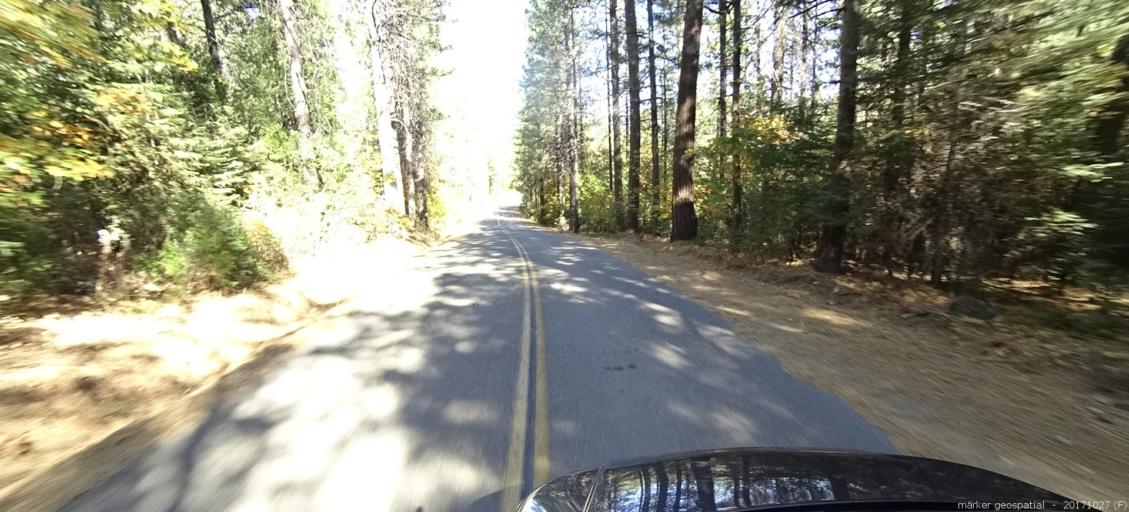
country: US
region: California
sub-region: Shasta County
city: Shingletown
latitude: 40.7280
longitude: -121.9302
